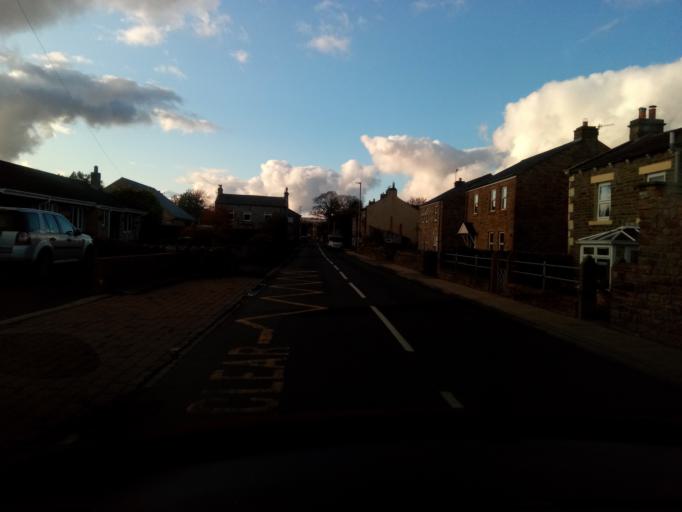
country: GB
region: England
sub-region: County Durham
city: Newbiggin
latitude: 54.7383
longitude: -2.1855
